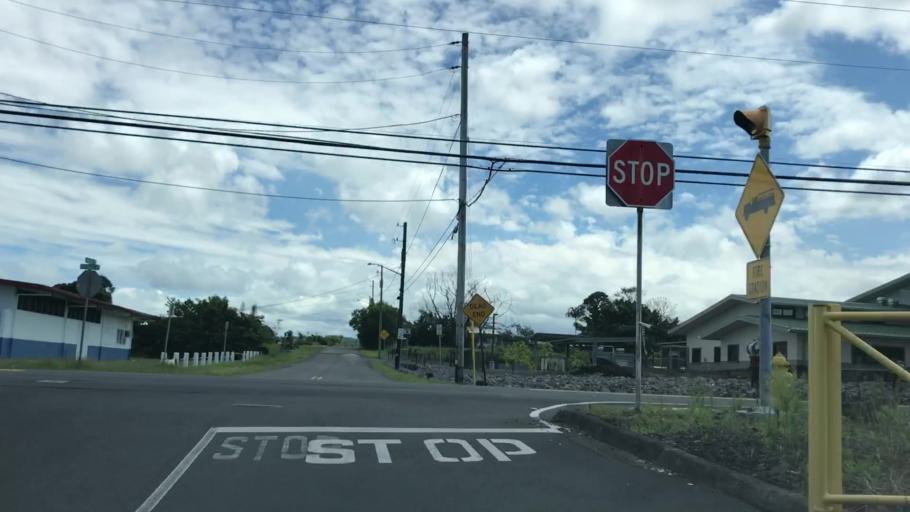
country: US
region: Hawaii
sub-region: Hawaii County
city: Hilo
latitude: 19.6741
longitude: -155.0776
